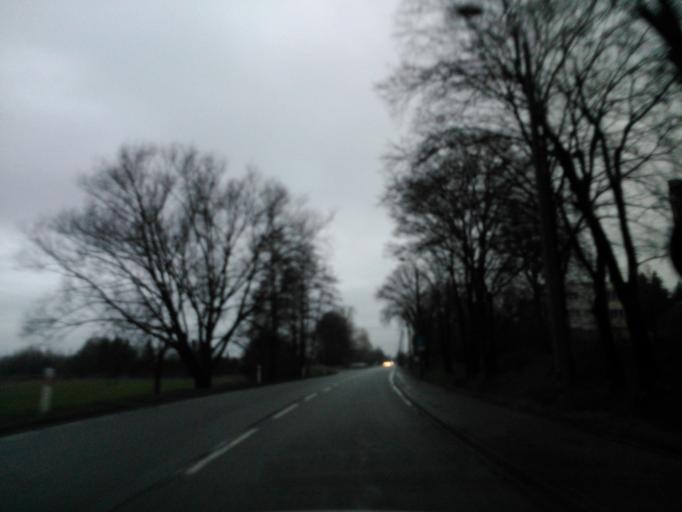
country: PL
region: Lublin Voivodeship
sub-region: Powiat krasnicki
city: Krasnik
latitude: 50.9118
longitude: 22.2522
